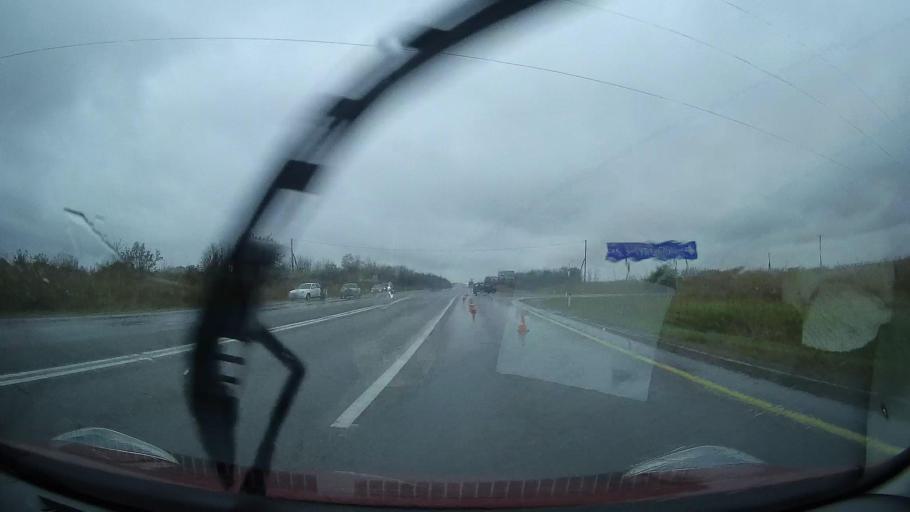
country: RU
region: Stavropol'skiy
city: Nevinnomyssk
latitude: 44.6342
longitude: 42.0072
